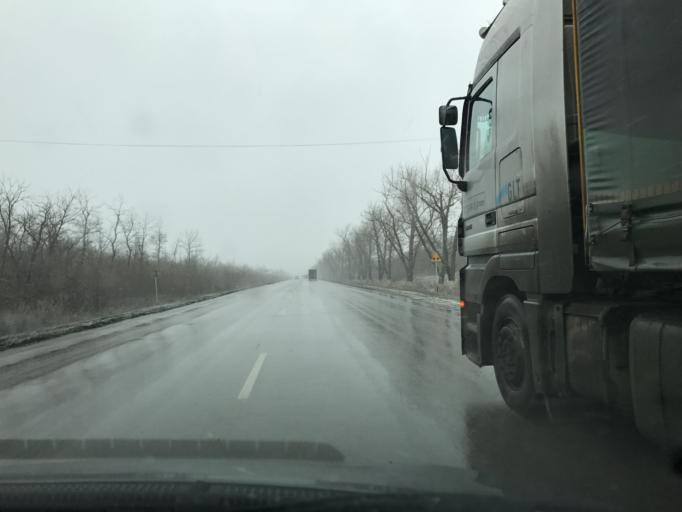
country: RU
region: Rostov
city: Bataysk
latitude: 47.0627
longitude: 39.8123
